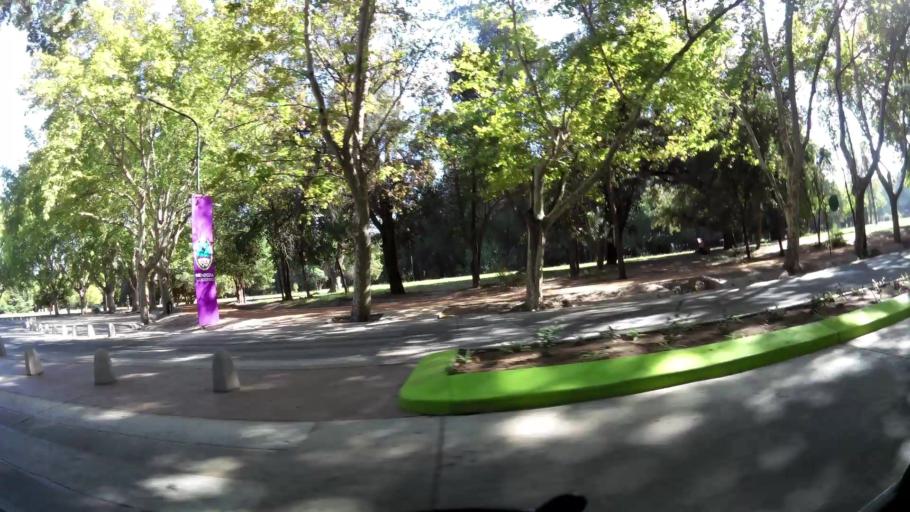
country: AR
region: Mendoza
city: Mendoza
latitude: -32.8890
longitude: -68.8659
